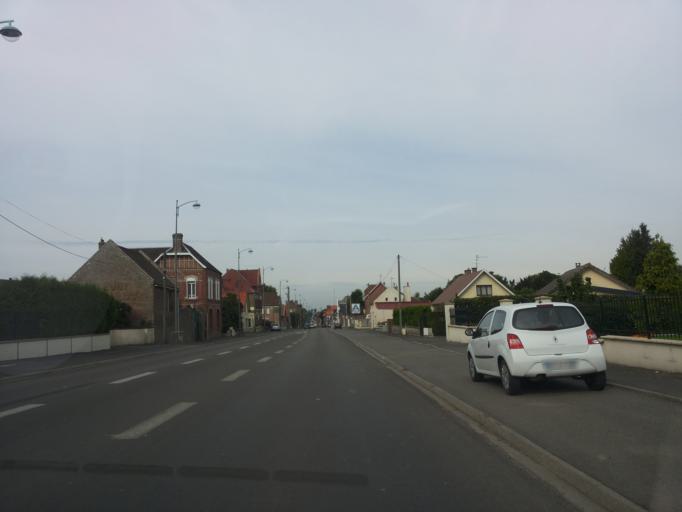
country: FR
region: Nord-Pas-de-Calais
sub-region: Departement du Pas-de-Calais
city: Marquion
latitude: 50.2095
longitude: 3.0927
